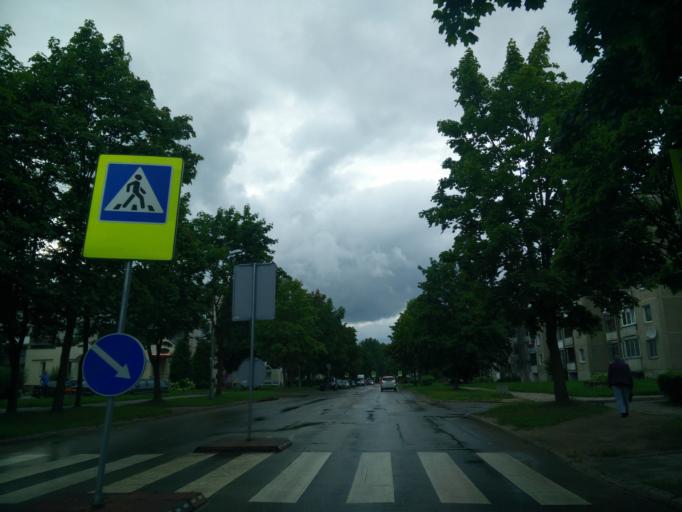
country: LT
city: Grigiskes
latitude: 54.6698
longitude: 25.0956
